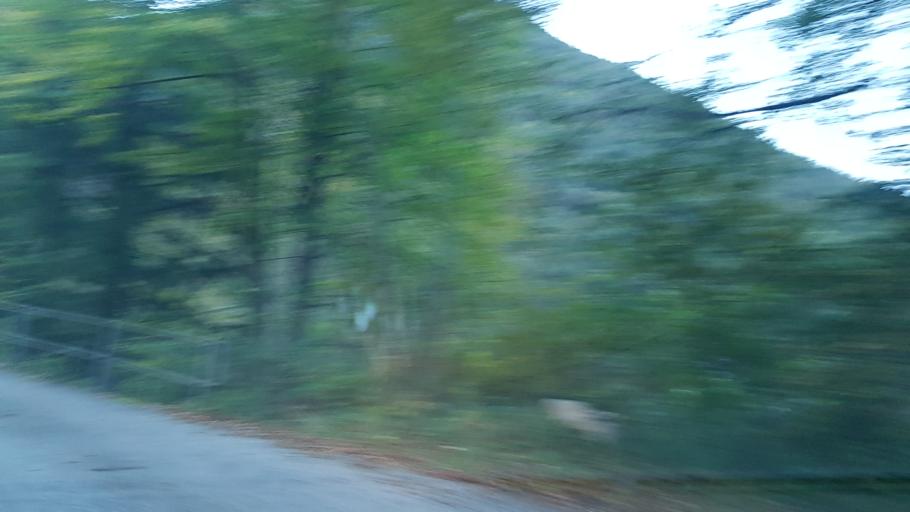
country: IT
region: Friuli Venezia Giulia
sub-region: Provincia di Udine
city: Venzone
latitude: 46.3334
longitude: 13.1513
